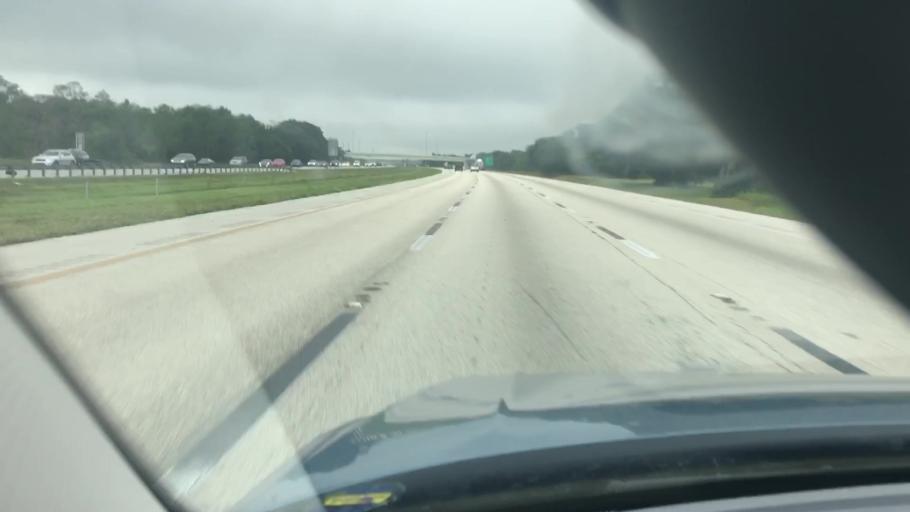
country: US
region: Florida
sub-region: Polk County
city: Polk City
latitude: 28.1575
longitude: -81.8354
